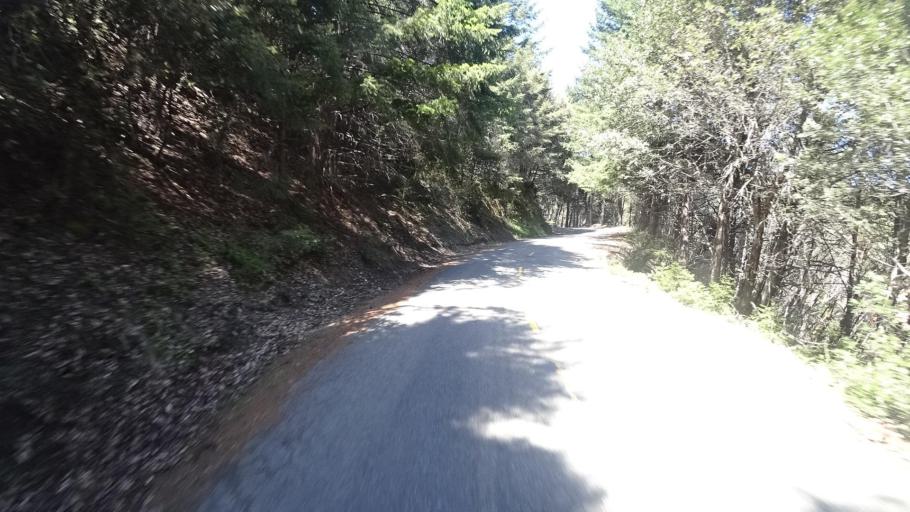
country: US
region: California
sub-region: Humboldt County
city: Rio Dell
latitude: 40.2708
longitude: -124.0779
